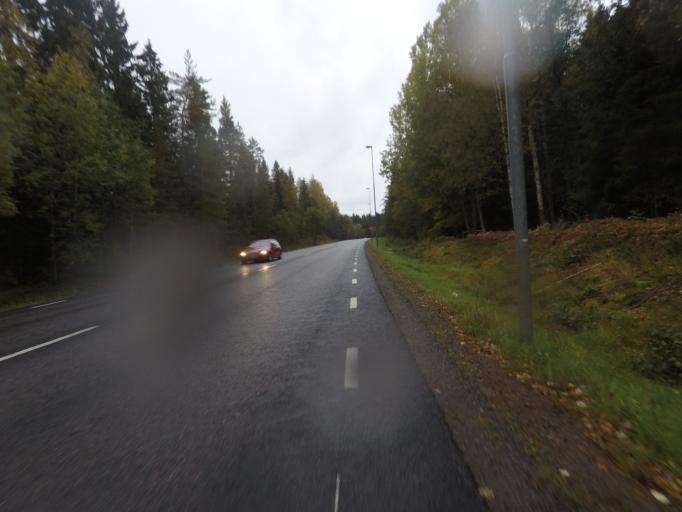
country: SE
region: OErebro
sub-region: Karlskoga Kommun
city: Karlskoga
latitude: 59.3094
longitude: 14.4680
